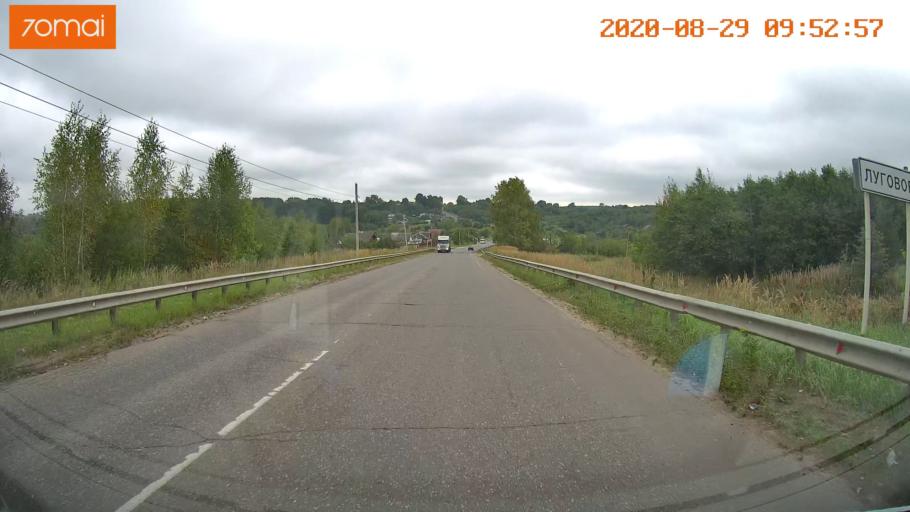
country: RU
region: Ivanovo
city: Zarechnyy
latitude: 57.4231
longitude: 42.2153
